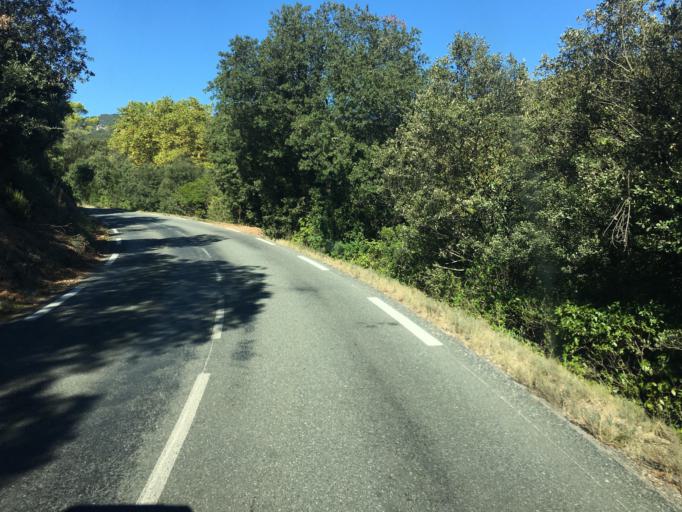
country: FR
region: Languedoc-Roussillon
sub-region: Departement de l'Herault
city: Nebian
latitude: 43.6121
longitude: 3.3807
